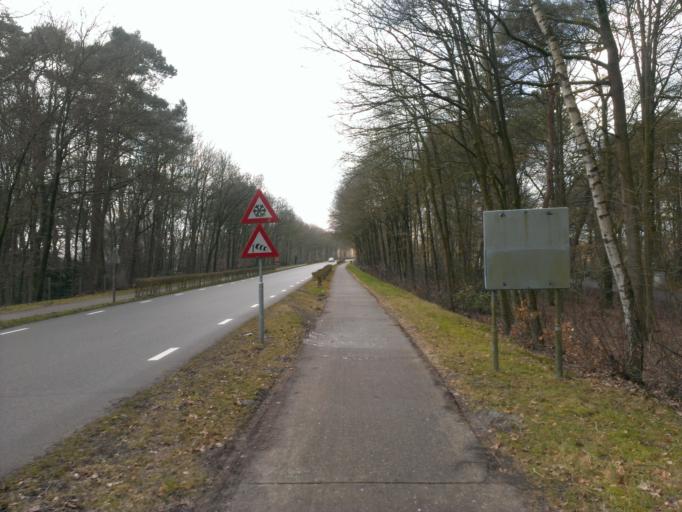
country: NL
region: Gelderland
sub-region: Gemeente Heerde
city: Heerde
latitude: 52.3873
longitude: 6.0209
